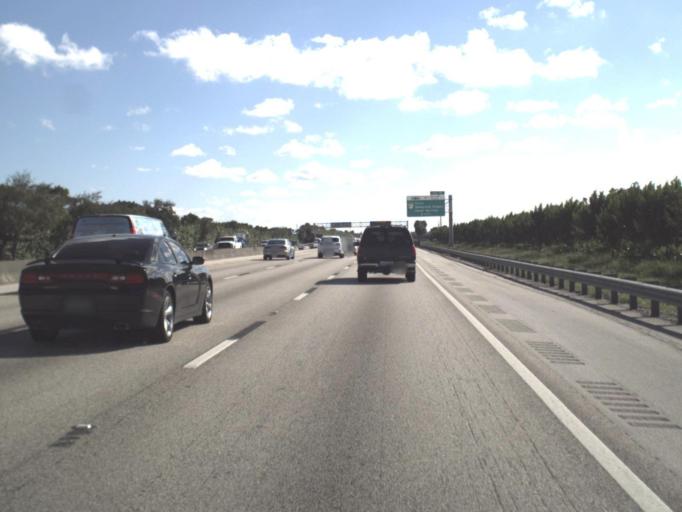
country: US
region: Florida
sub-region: Palm Beach County
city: Boca Pointe
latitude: 26.3410
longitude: -80.1706
